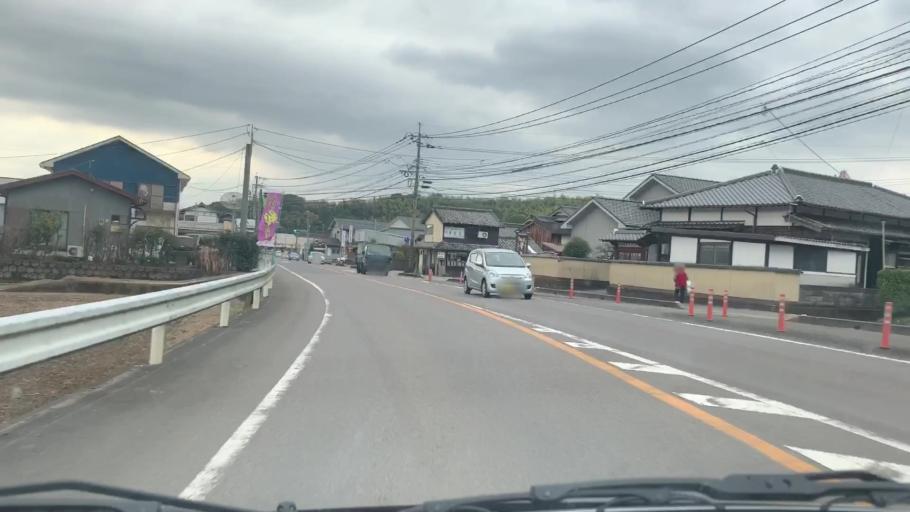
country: JP
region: Saga Prefecture
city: Kashima
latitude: 33.1491
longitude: 130.0632
